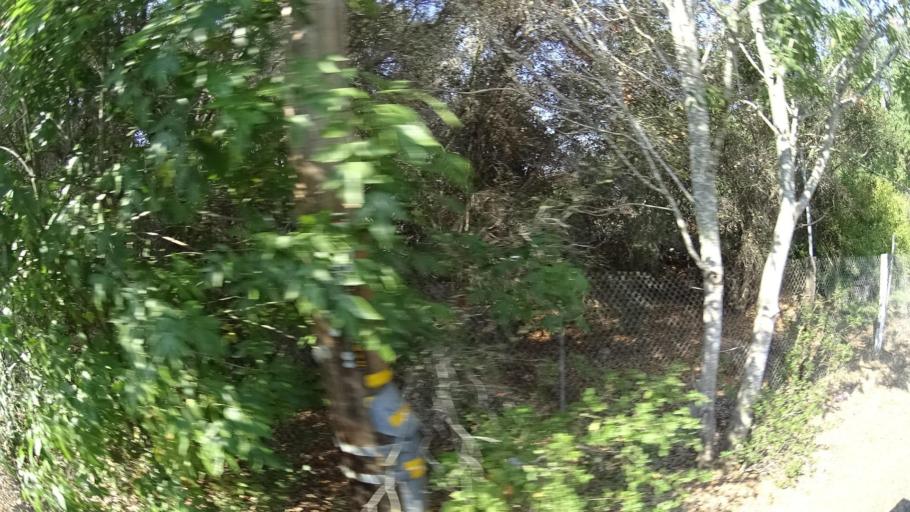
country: US
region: California
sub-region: San Diego County
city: Vista
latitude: 33.2298
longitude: -117.2324
